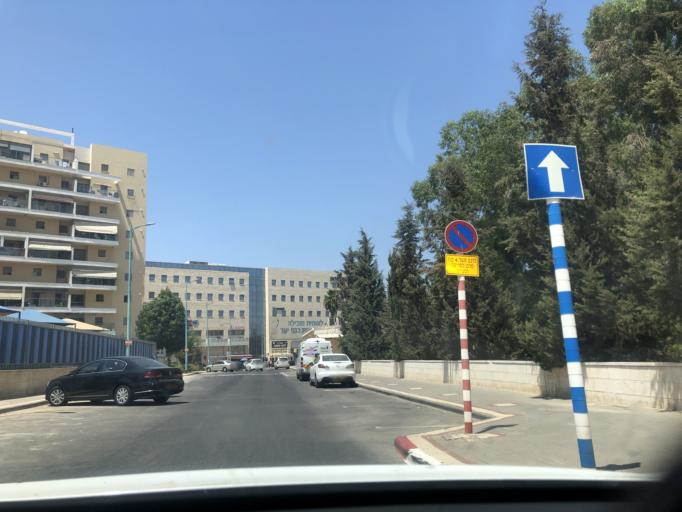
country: IL
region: Central District
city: Lod
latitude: 31.9438
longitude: 34.9012
